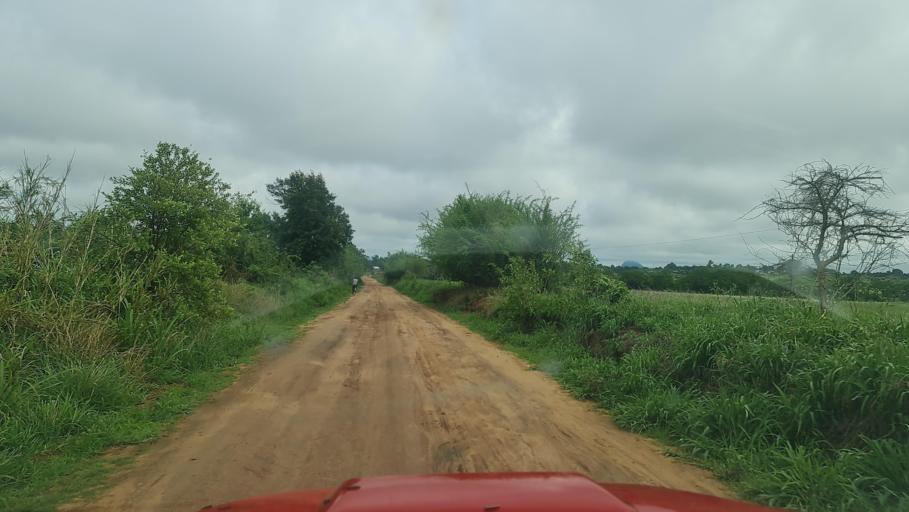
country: MW
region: Southern Region
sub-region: Nsanje District
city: Nsanje
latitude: -17.1966
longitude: 35.7008
